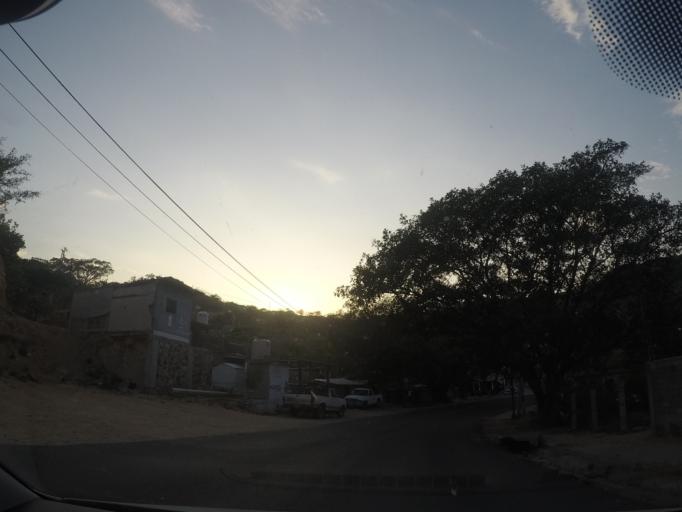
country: MX
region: Oaxaca
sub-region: Salina Cruz
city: Salina Cruz
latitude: 16.1918
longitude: -95.2096
